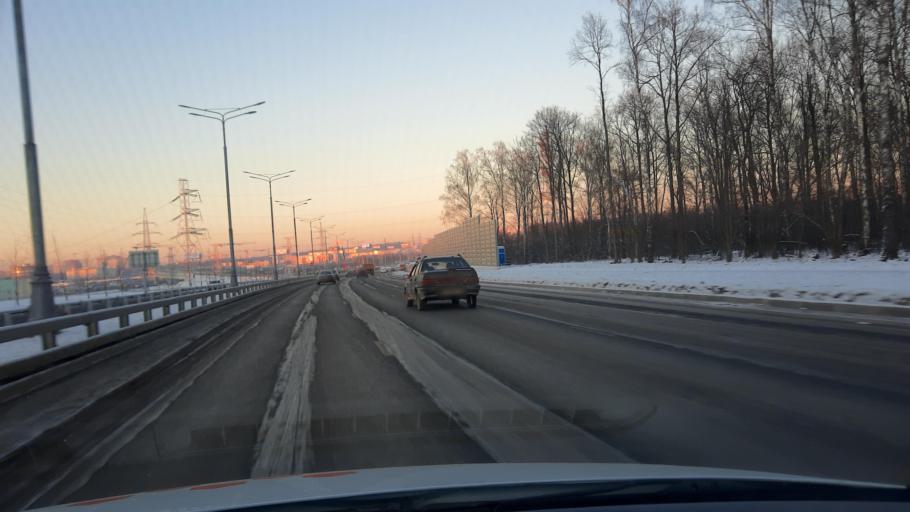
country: RU
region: Moskovskaya
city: Kommunarka
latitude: 55.5905
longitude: 37.4816
